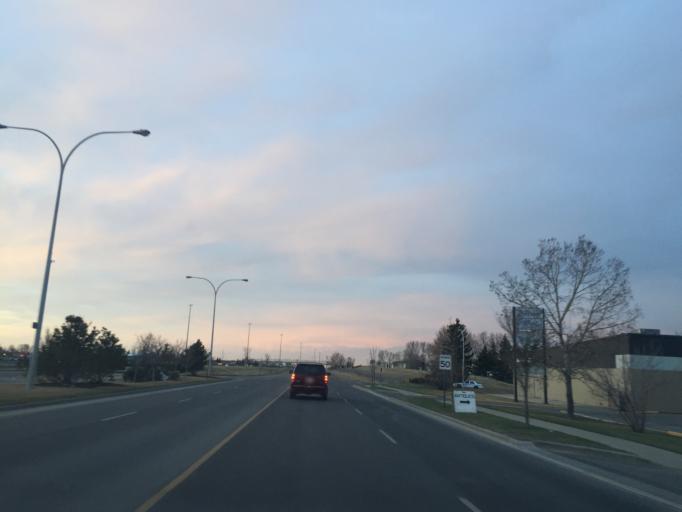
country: CA
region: Alberta
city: Airdrie
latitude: 51.2899
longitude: -114.0017
